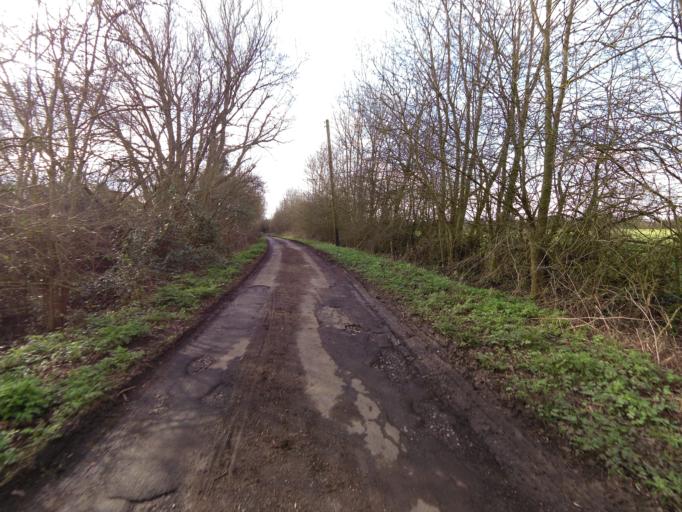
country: GB
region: England
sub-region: East Riding of Yorkshire
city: Pollington
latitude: 53.6490
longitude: -1.0607
